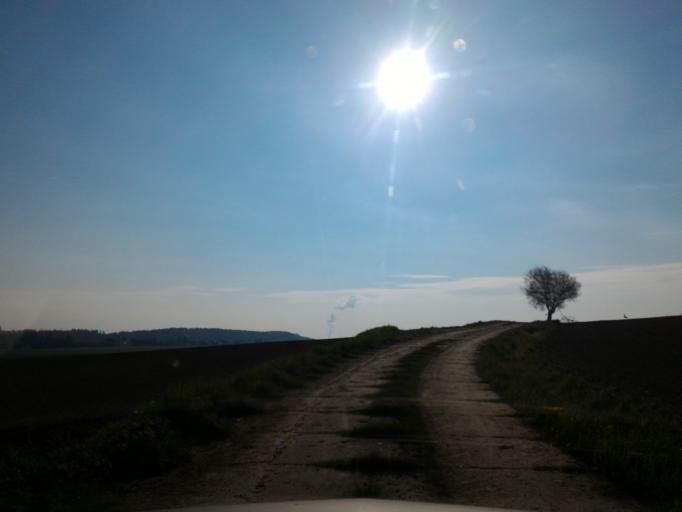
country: DE
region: Saxony
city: Leutersdorf
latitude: 50.9457
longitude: 14.6581
